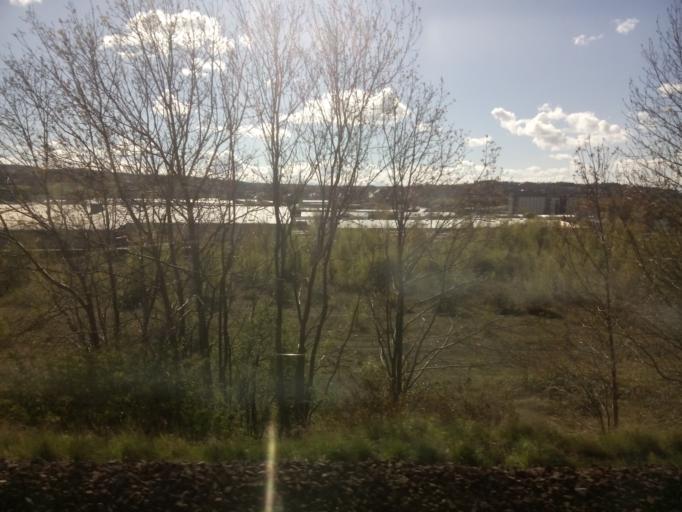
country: GB
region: England
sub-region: Gateshead
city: Gateshead
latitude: 54.9434
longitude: -1.6128
